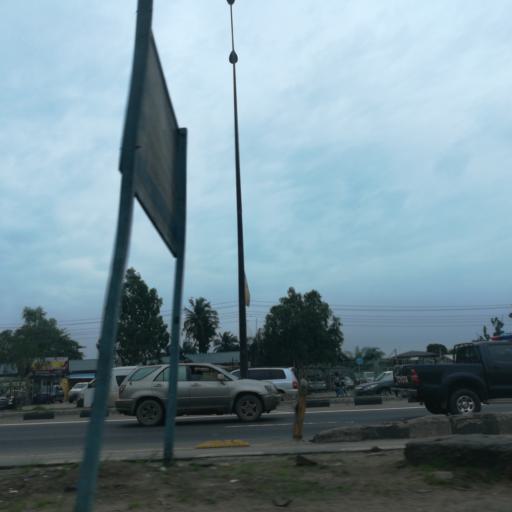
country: NG
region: Lagos
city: Ojota
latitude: 6.5648
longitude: 3.3669
